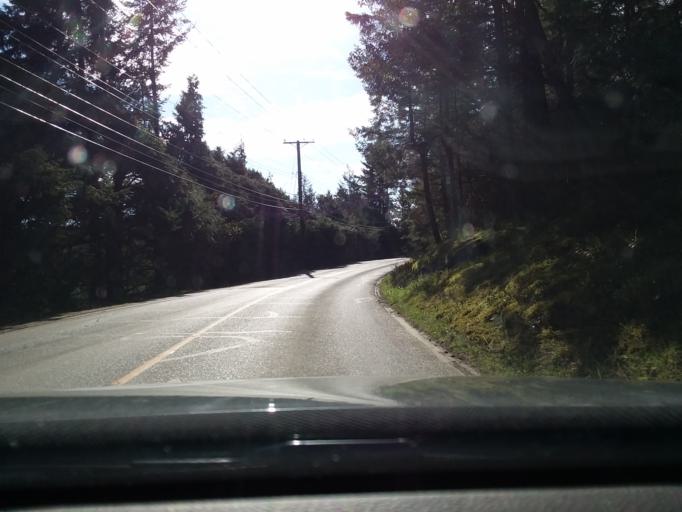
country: CA
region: British Columbia
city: North Saanich
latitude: 48.8830
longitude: -123.3278
